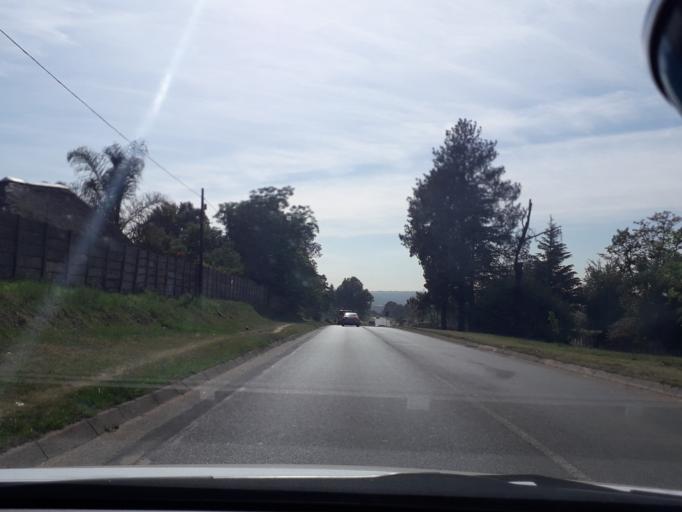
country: ZA
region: Gauteng
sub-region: City of Johannesburg Metropolitan Municipality
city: Roodepoort
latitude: -26.1187
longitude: 27.9309
